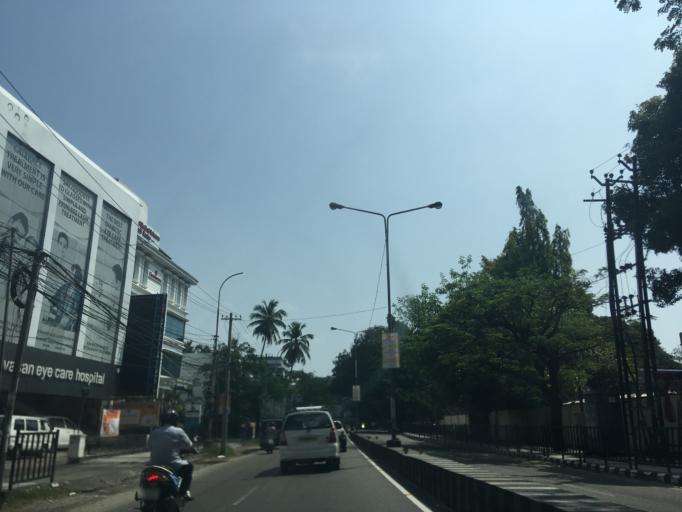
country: IN
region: Kerala
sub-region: Ernakulam
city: Cochin
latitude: 9.9549
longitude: 76.2925
